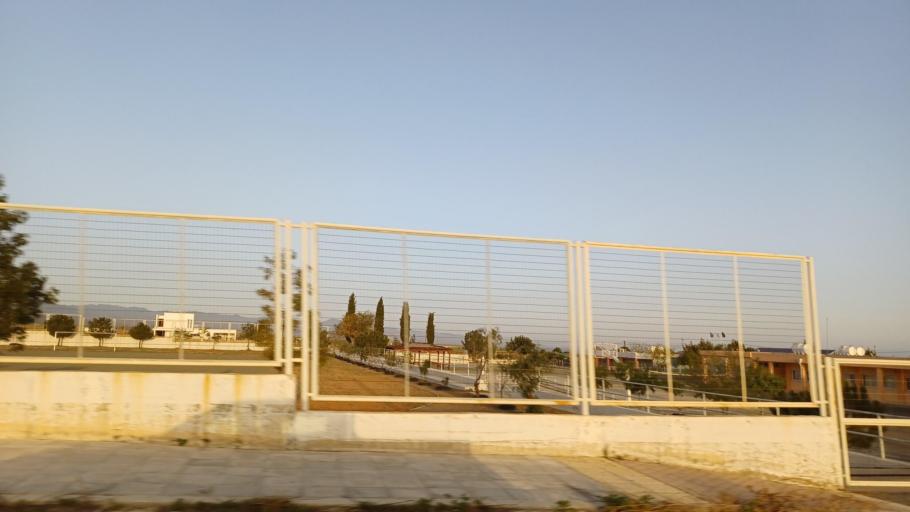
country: CY
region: Lefkosia
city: Astromeritis
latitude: 35.0932
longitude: 33.0154
